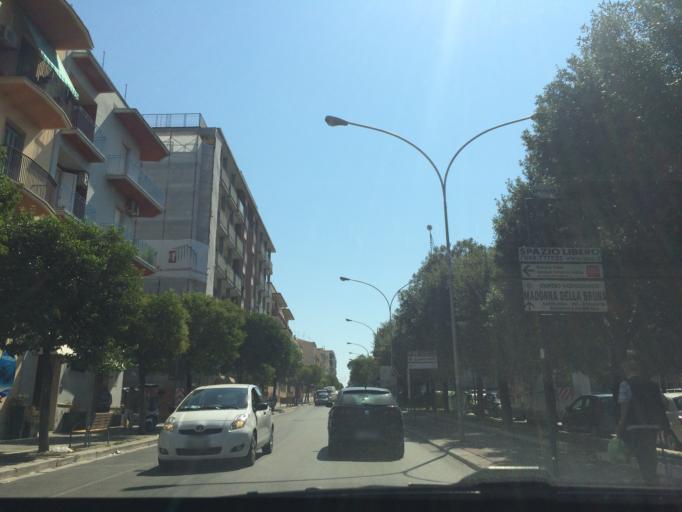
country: IT
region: Basilicate
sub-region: Provincia di Matera
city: Matera
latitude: 40.6744
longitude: 16.5982
